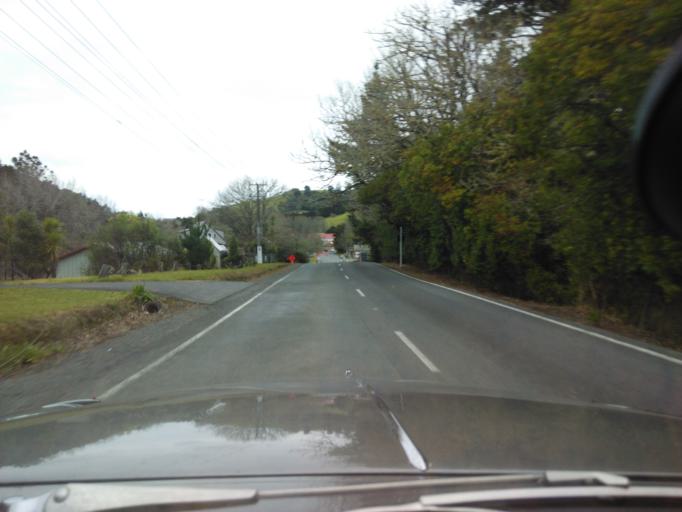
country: NZ
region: Auckland
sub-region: Auckland
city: Warkworth
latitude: -36.5102
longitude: 174.6602
